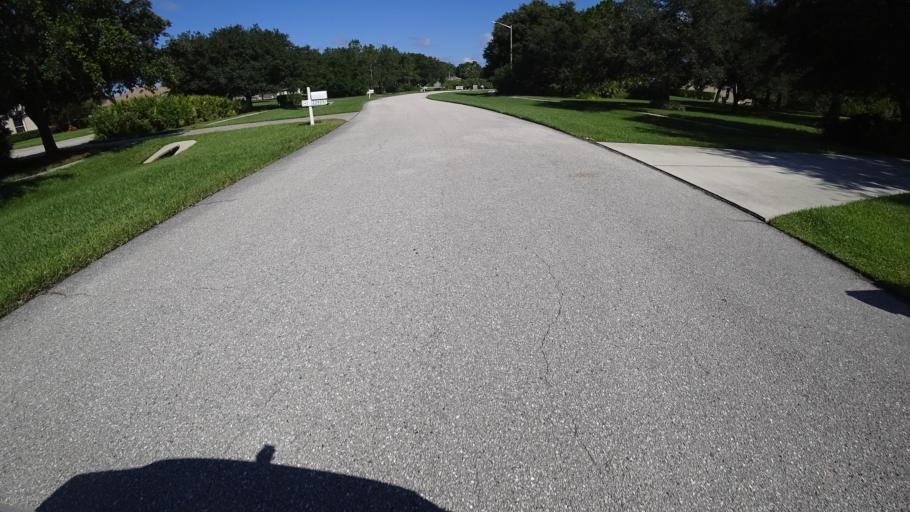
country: US
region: Florida
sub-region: Sarasota County
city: Fruitville
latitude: 27.3947
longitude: -82.3184
